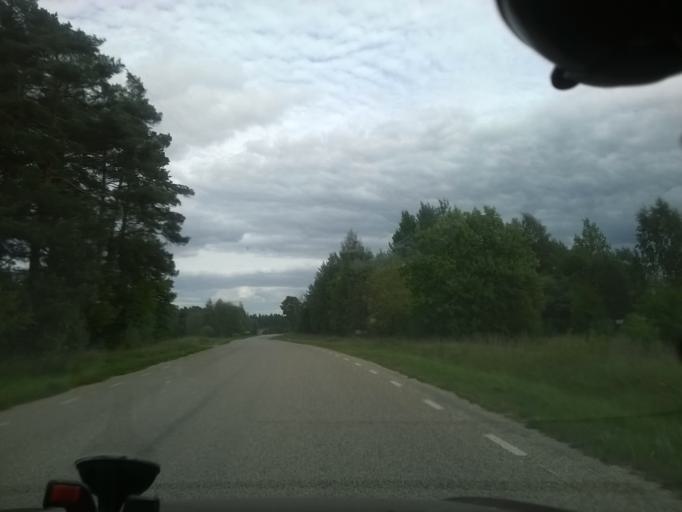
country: EE
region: Vorumaa
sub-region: Voru linn
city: Voru
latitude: 57.7500
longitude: 26.9712
